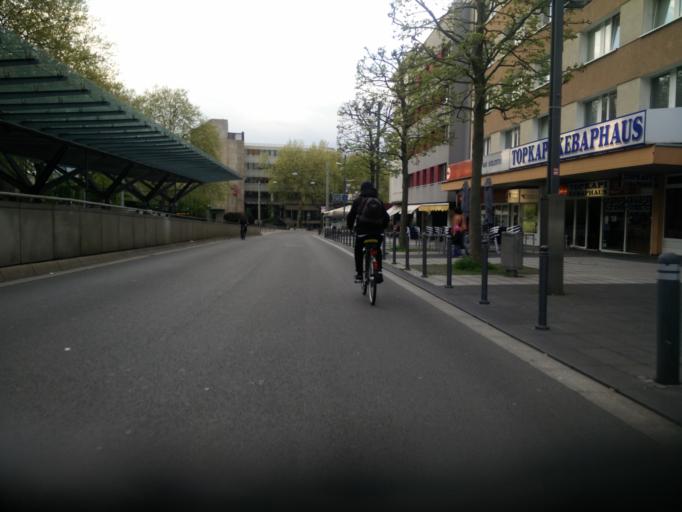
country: DE
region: North Rhine-Westphalia
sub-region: Regierungsbezirk Arnsberg
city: Bochum
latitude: 51.4825
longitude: 7.2160
